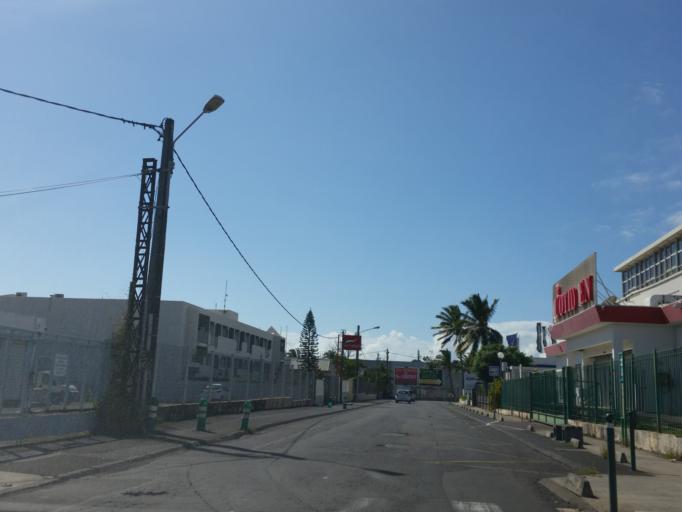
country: RE
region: Reunion
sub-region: Reunion
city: Saint-Denis
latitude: -20.8953
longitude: 55.4964
